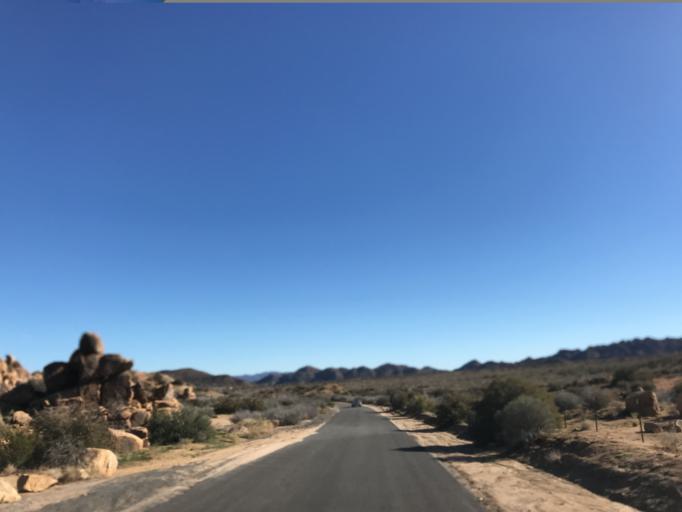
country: US
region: California
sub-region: San Bernardino County
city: Yucca Valley
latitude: 34.1863
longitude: -116.5442
